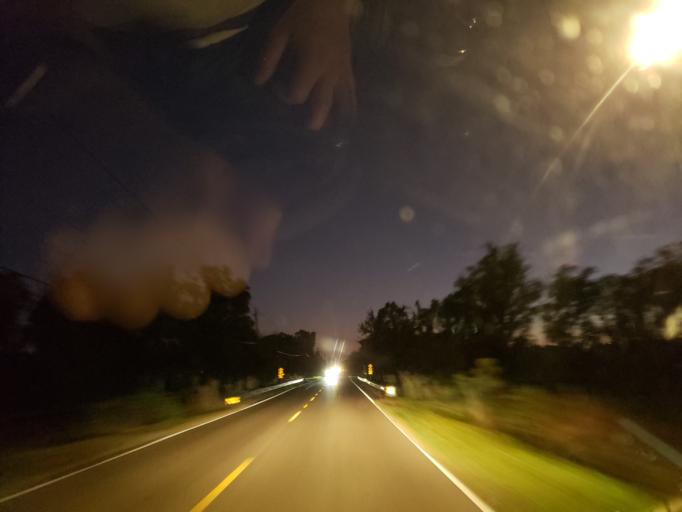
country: US
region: Florida
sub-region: Hillsborough County
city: Dover
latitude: 27.9896
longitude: -82.2198
